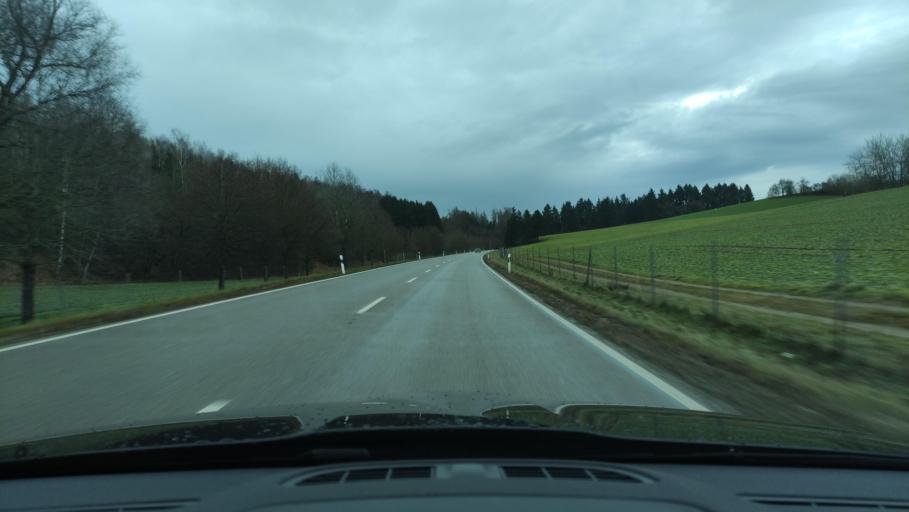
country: DE
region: Bavaria
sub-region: Swabia
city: Thannhausen
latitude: 48.2939
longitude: 10.4735
